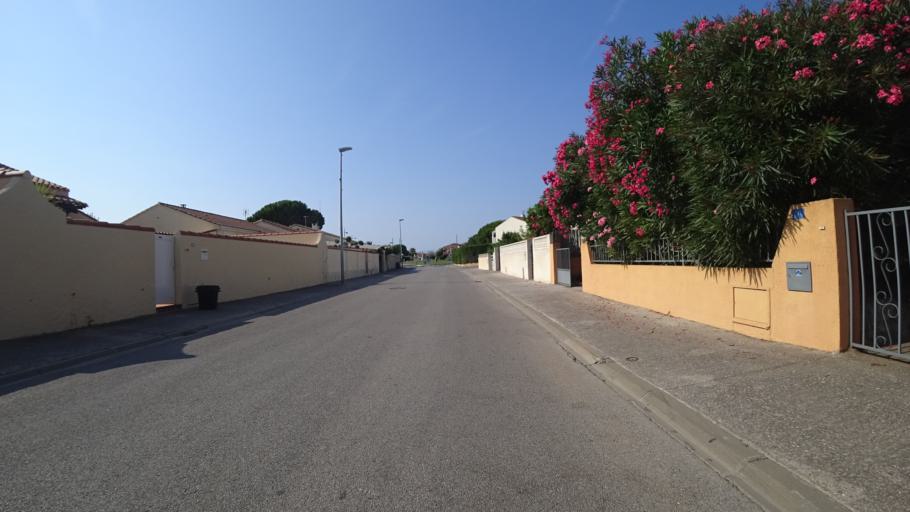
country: FR
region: Languedoc-Roussillon
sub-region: Departement des Pyrenees-Orientales
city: Saint-Laurent-de-la-Salanque
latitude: 42.7741
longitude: 3.0103
